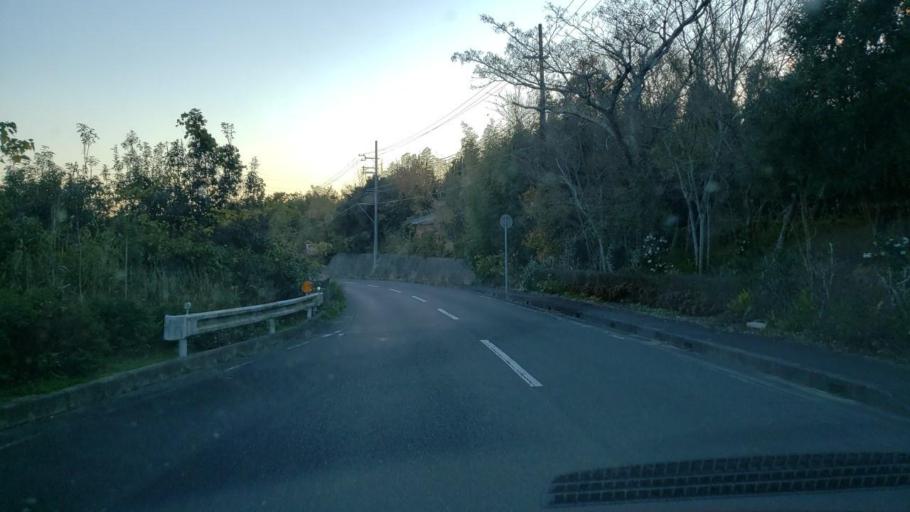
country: JP
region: Hyogo
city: Sumoto
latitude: 34.3591
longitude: 134.7849
